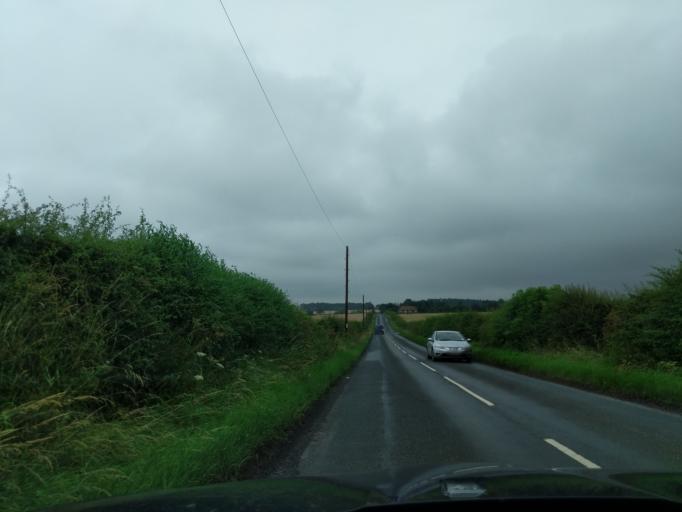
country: GB
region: England
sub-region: Northumberland
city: Ford
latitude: 55.6651
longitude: -2.1017
